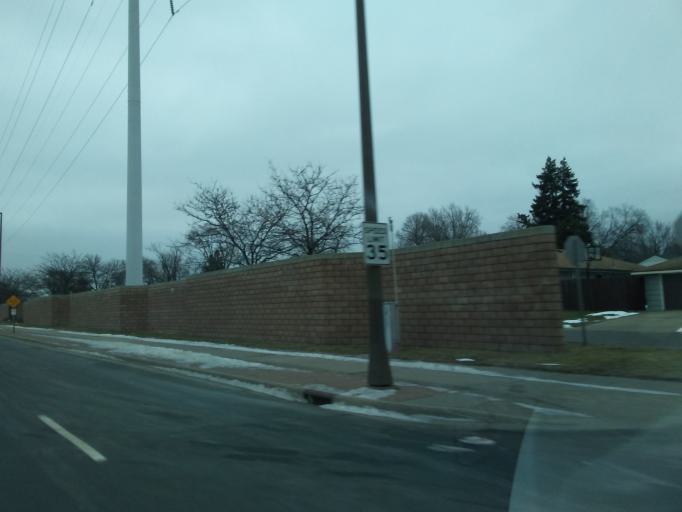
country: US
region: Minnesota
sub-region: Hennepin County
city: Richfield
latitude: 44.8596
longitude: -93.2727
